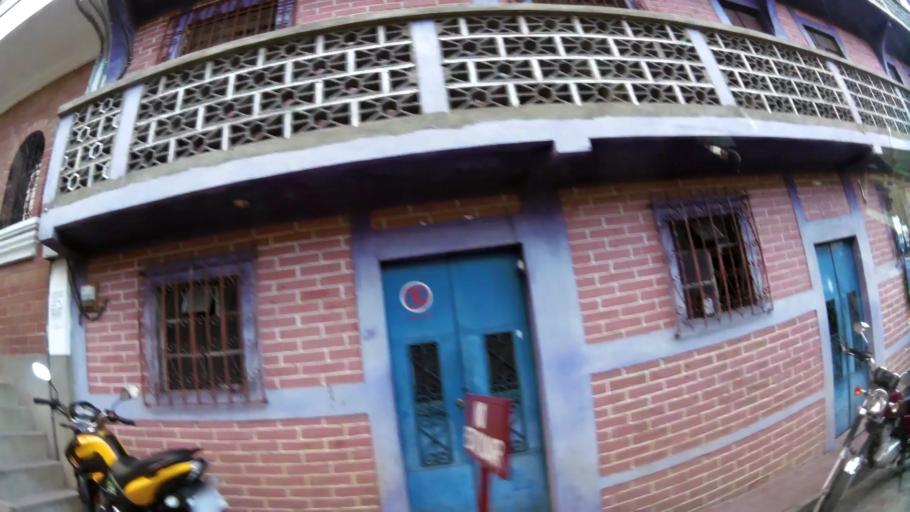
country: GT
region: Quiche
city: Chichicastenango
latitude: 14.9400
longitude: -91.1125
